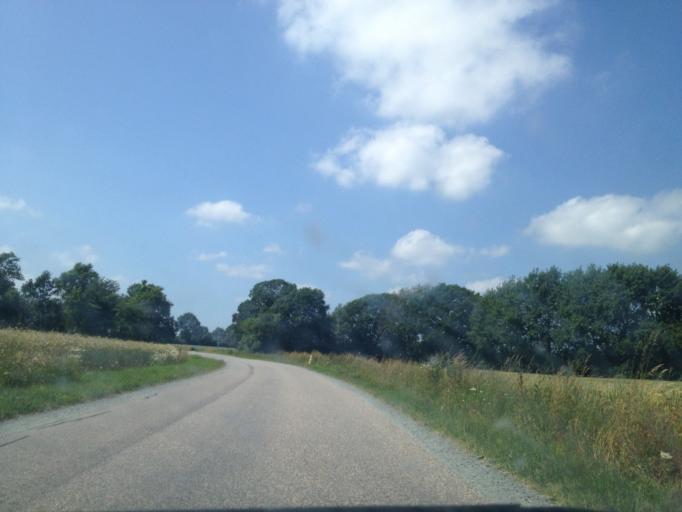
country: DK
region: South Denmark
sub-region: Kolding Kommune
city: Vamdrup
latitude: 55.3880
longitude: 9.2525
